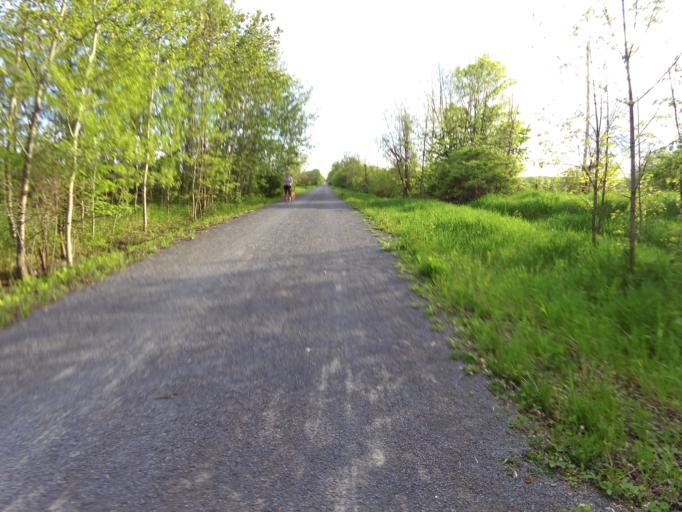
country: CA
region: Ontario
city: Bells Corners
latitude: 45.3220
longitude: -75.8406
